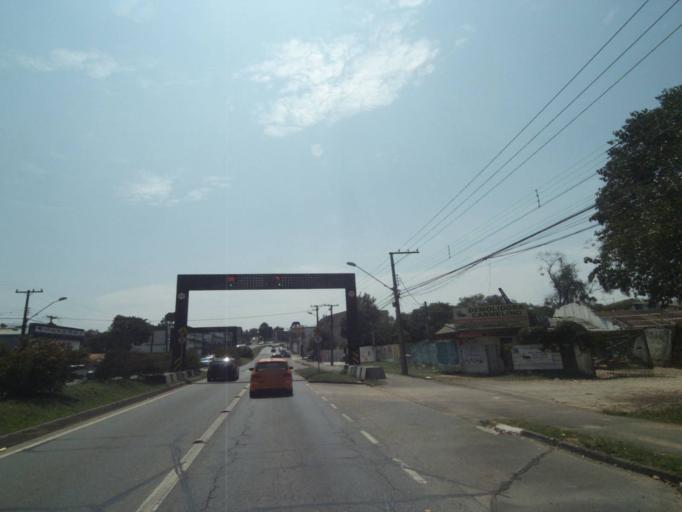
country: BR
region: Parana
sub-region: Curitiba
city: Curitiba
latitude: -25.4811
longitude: -49.3155
